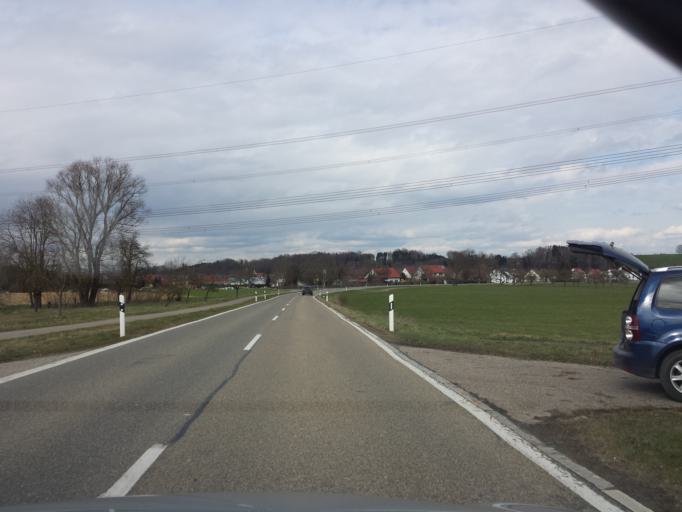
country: DE
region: Baden-Wuerttemberg
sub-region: Tuebingen Region
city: Huttisheim
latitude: 48.2736
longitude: 9.9383
